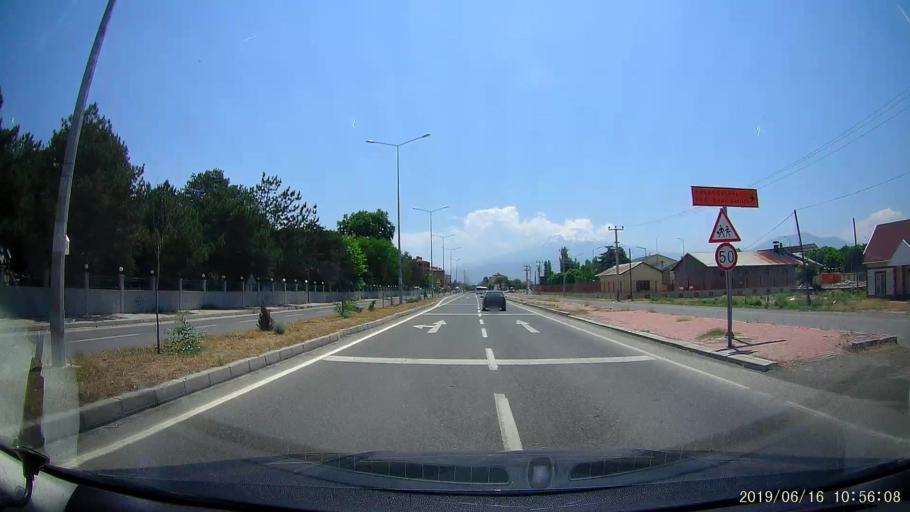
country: TR
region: Igdir
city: Igdir
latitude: 39.9320
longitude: 44.0184
